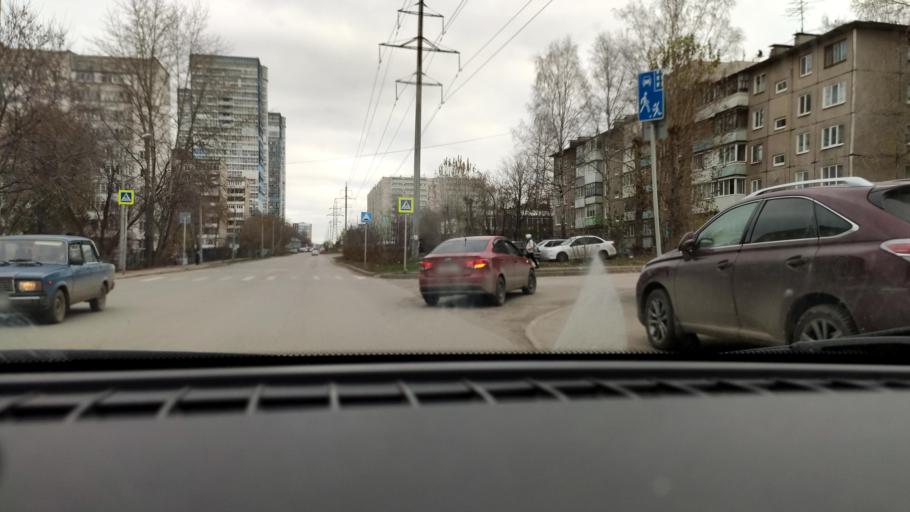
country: RU
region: Perm
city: Kondratovo
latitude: 57.9679
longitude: 56.1633
